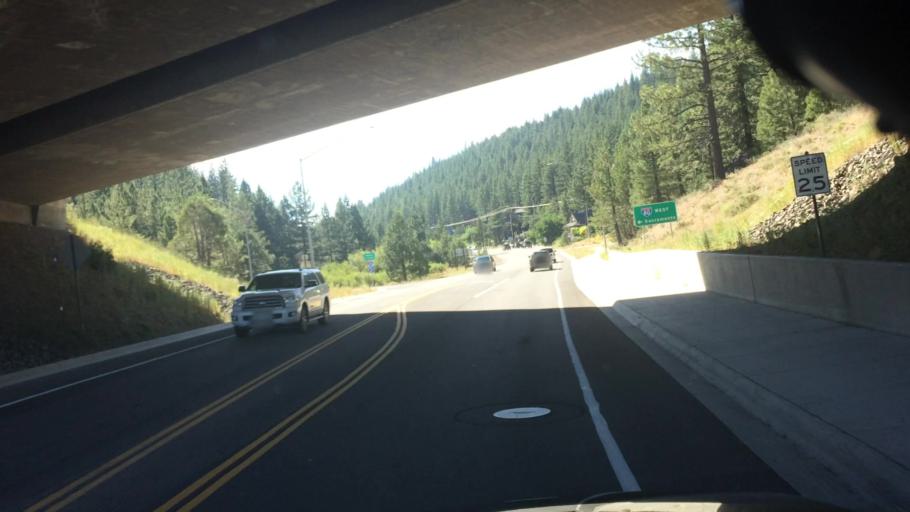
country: US
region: California
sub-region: Nevada County
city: Truckee
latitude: 39.3257
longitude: -120.1931
